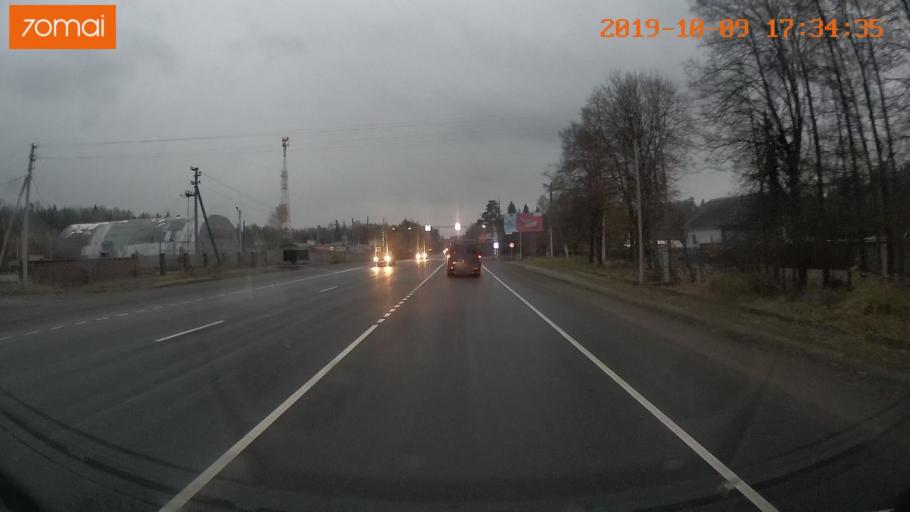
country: RU
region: Ivanovo
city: Bogorodskoye
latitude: 57.1052
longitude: 41.0103
